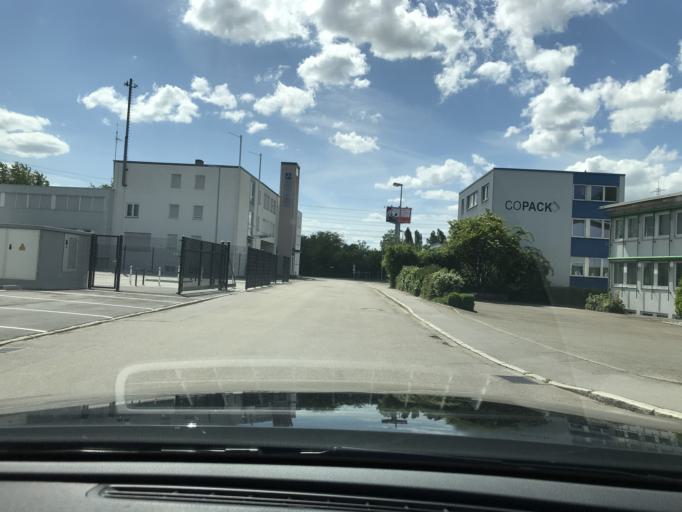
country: DE
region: Baden-Wuerttemberg
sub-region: Regierungsbezirk Stuttgart
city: Weinstadt-Endersbach
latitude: 48.8161
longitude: 9.3829
